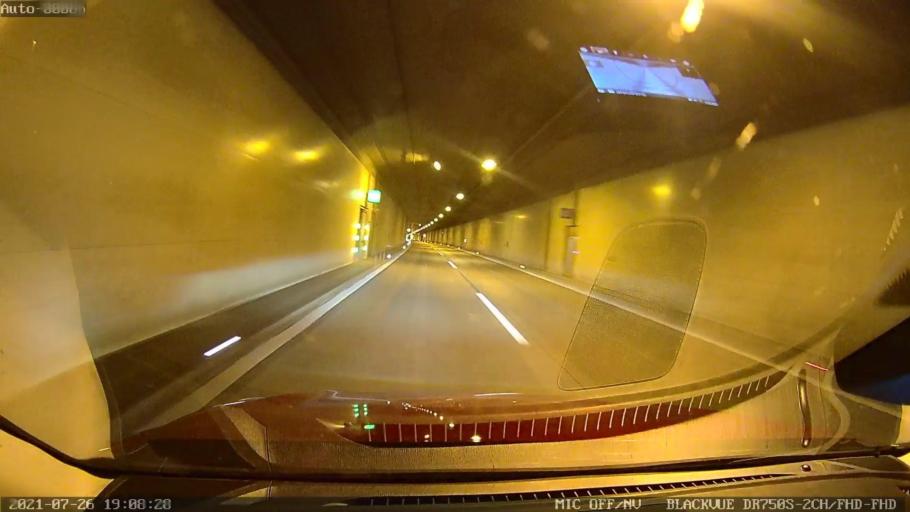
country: AT
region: Upper Austria
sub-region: Wels-Land
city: Steinhaus
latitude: 48.1106
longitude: 14.0135
